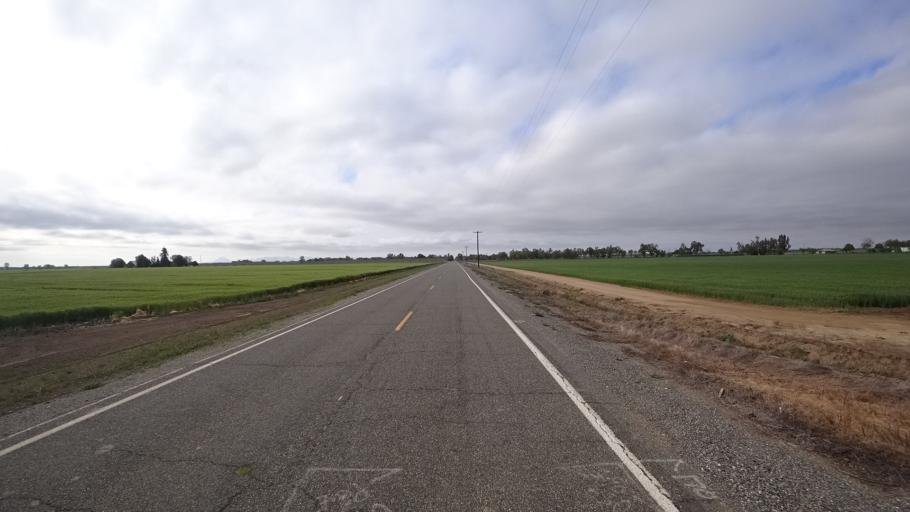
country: US
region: California
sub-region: Colusa County
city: Colusa
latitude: 39.4310
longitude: -121.9669
